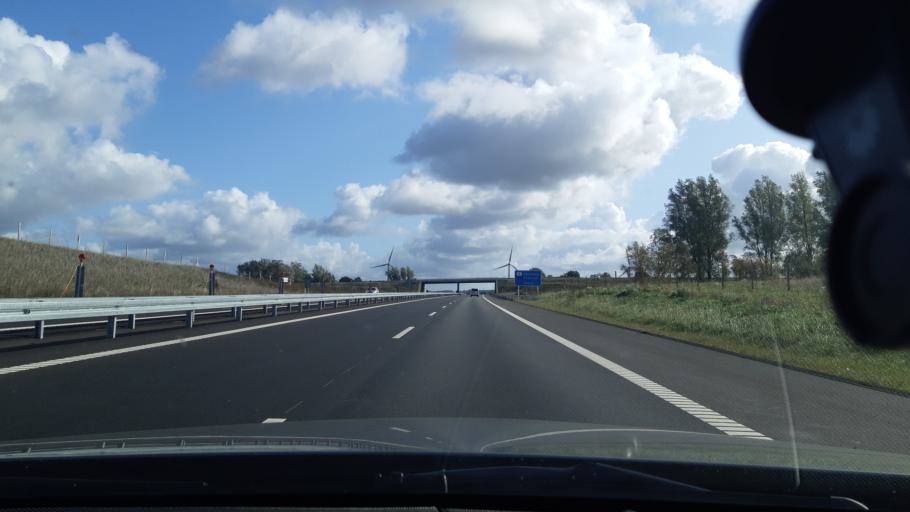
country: DK
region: Zealand
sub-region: Holbaek Kommune
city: Holbaek
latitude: 55.6605
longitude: 11.6126
